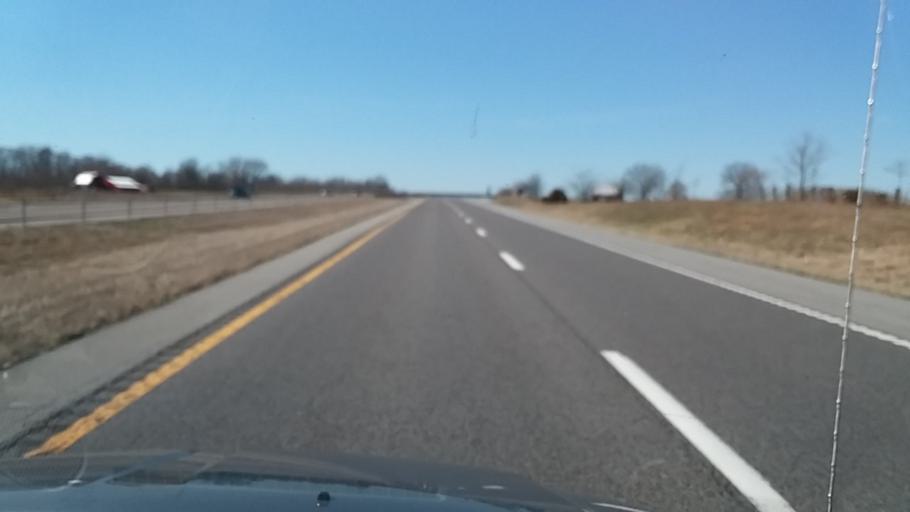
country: US
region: Missouri
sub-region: Cape Girardeau County
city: Jackson
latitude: 37.5463
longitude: -89.7301
